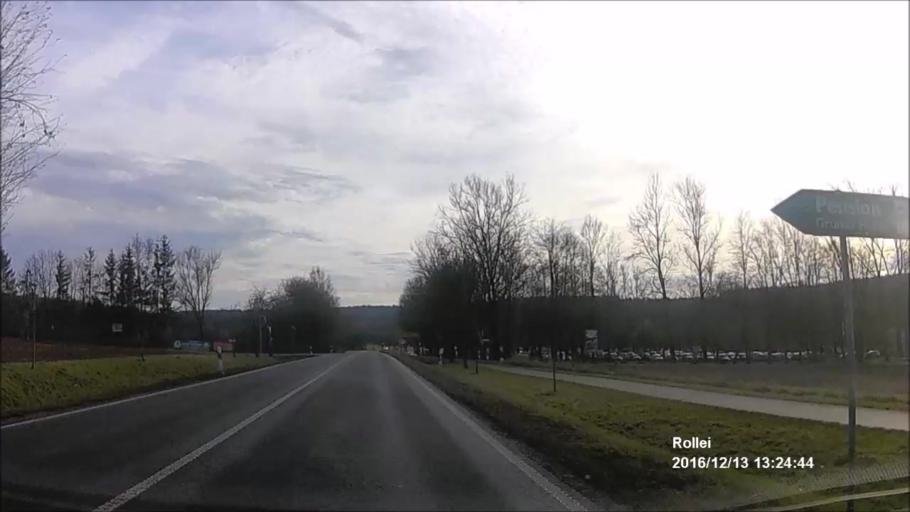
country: DE
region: Thuringia
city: Nauendorf
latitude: 50.8805
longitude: 11.1856
